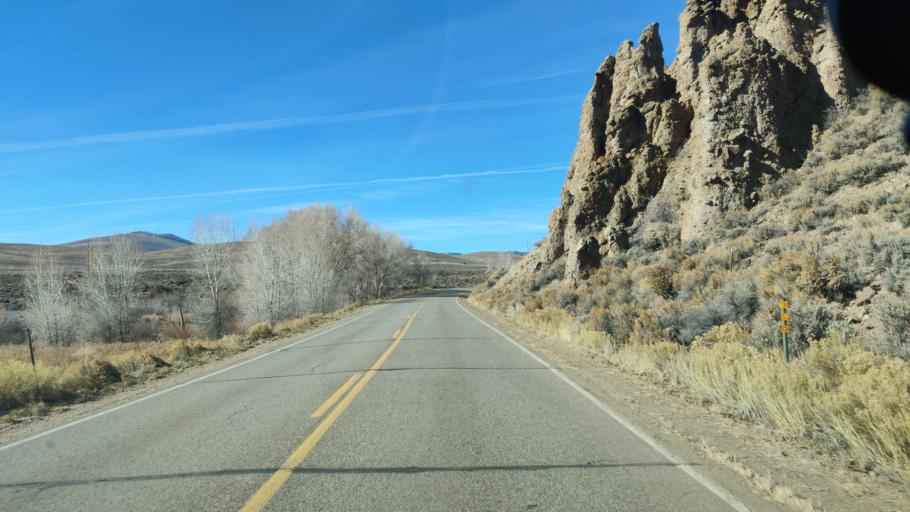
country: US
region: Colorado
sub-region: Gunnison County
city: Gunnison
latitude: 38.5596
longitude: -106.9547
